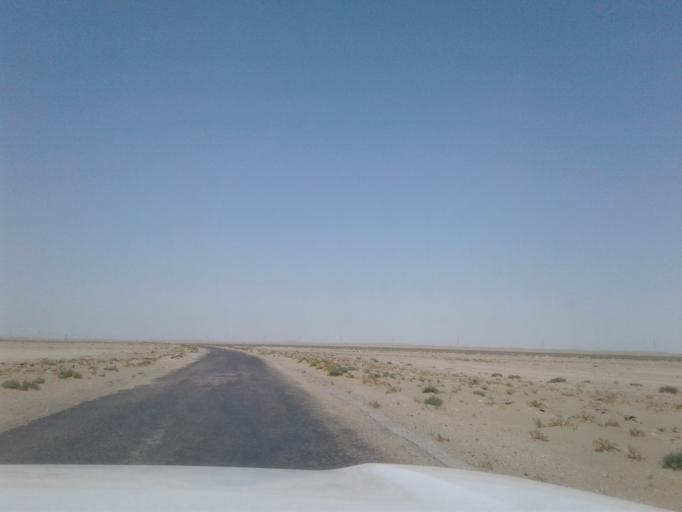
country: TM
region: Balkan
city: Gumdag
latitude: 38.3885
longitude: 54.3987
